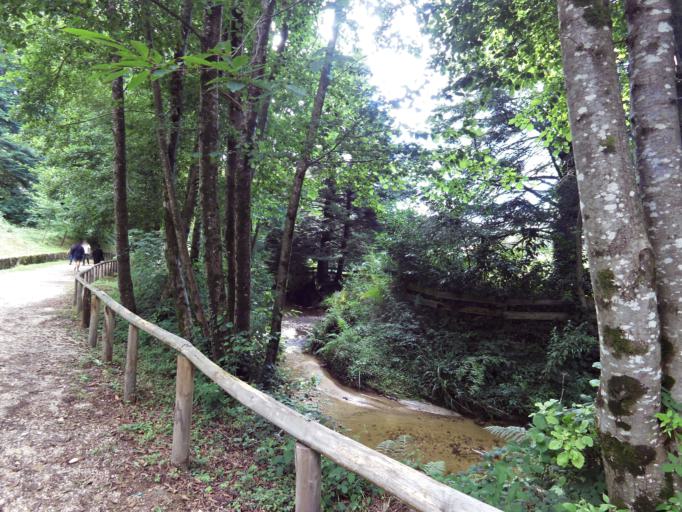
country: IT
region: Calabria
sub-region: Provincia di Vibo-Valentia
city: Serra San Bruno
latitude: 38.5594
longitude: 16.3167
